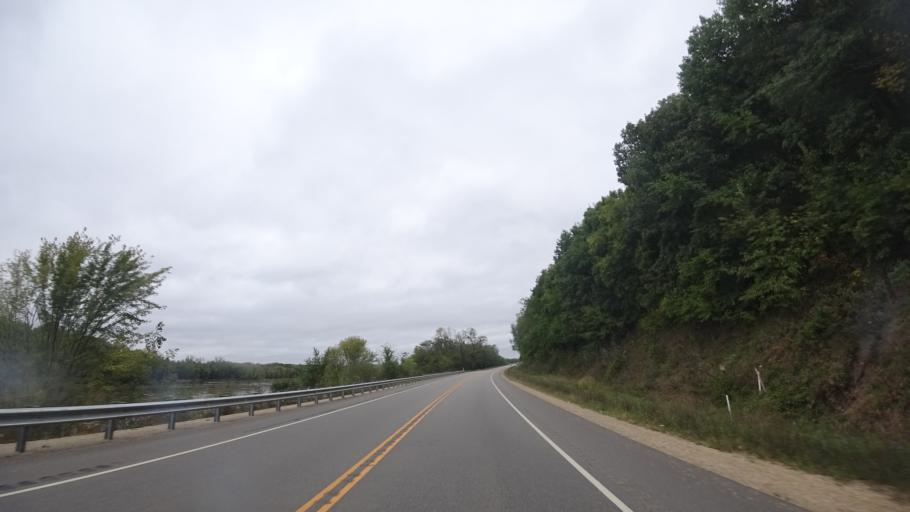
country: US
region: Wisconsin
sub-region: Grant County
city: Boscobel
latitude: 43.1592
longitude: -90.7090
